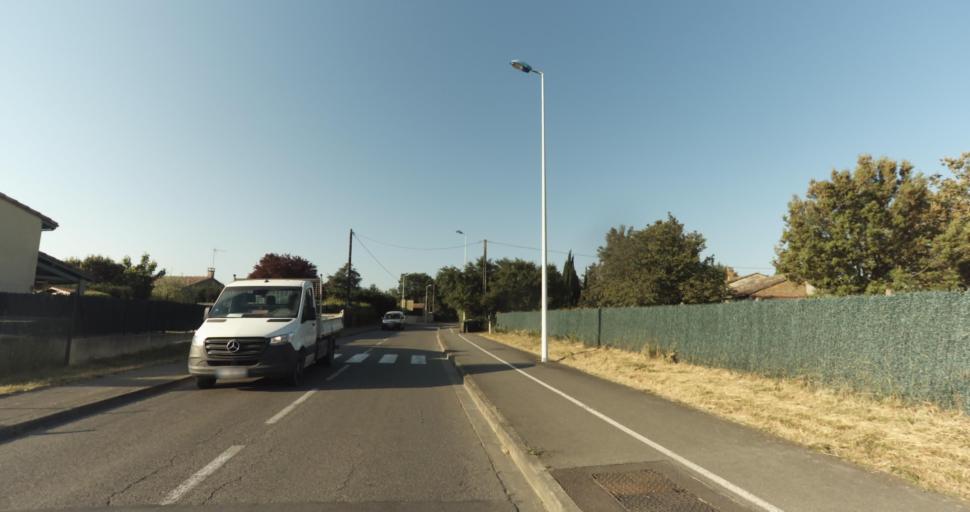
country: FR
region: Midi-Pyrenees
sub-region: Departement de la Haute-Garonne
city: Leguevin
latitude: 43.6066
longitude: 1.2342
